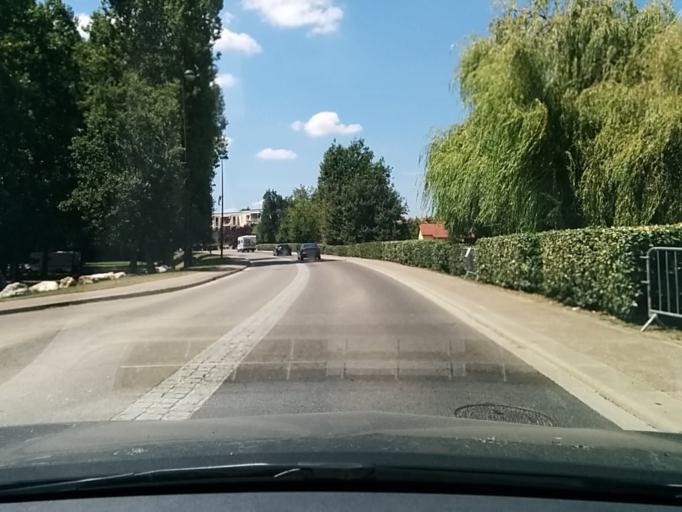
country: FR
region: Midi-Pyrenees
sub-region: Departement du Gers
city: Vic-Fezensac
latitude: 43.7555
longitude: 0.3055
